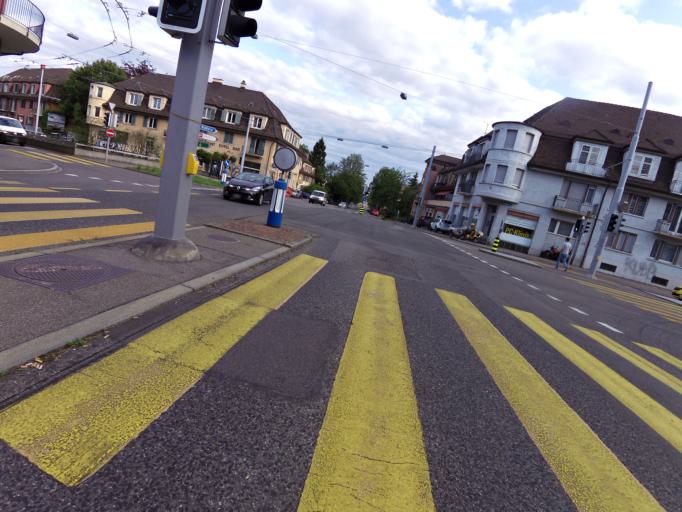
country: CH
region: Zurich
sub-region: Bezirk Zuerich
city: Zuerich (Kreis 6) / Unterstrass
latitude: 47.3985
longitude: 8.5393
